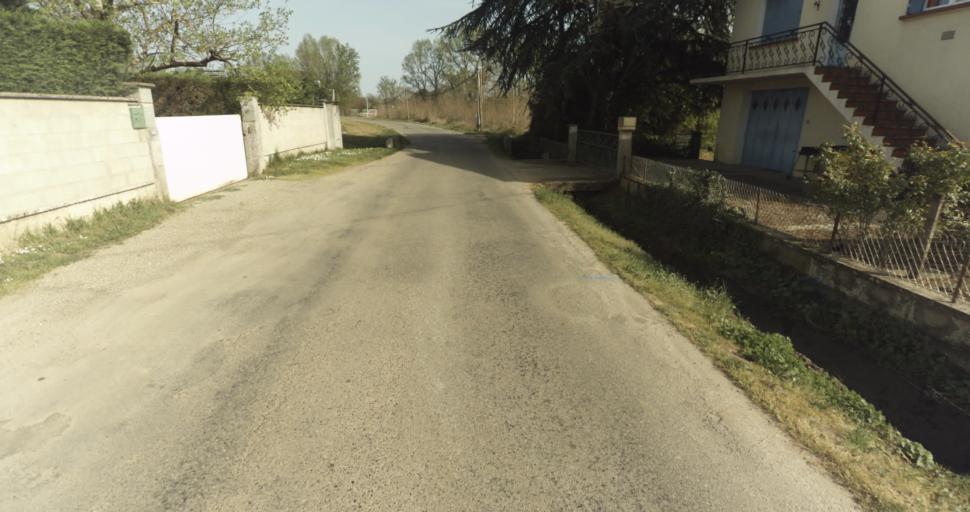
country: FR
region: Midi-Pyrenees
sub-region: Departement du Tarn-et-Garonne
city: Moissac
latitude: 44.1203
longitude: 1.1526
